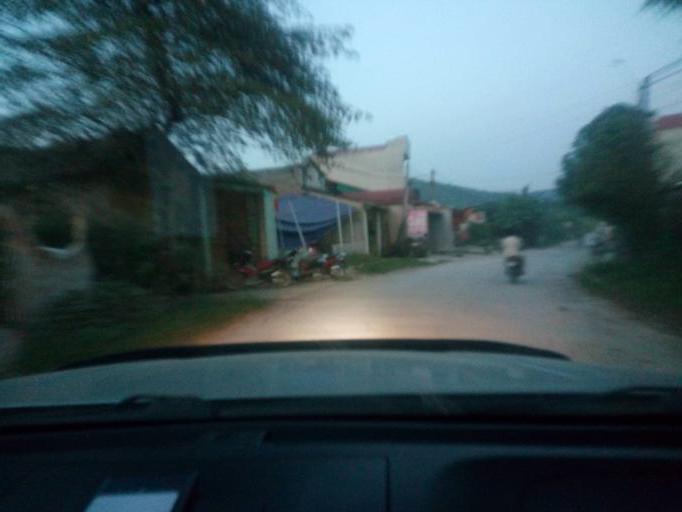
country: VN
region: Yen Bai
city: Co Phuc
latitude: 21.8660
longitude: 104.6461
